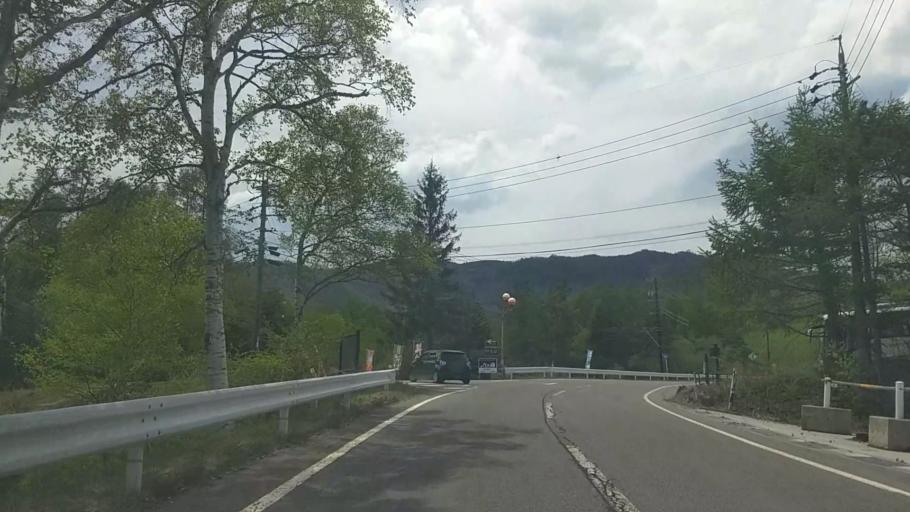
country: JP
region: Nagano
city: Saku
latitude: 36.0778
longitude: 138.3851
